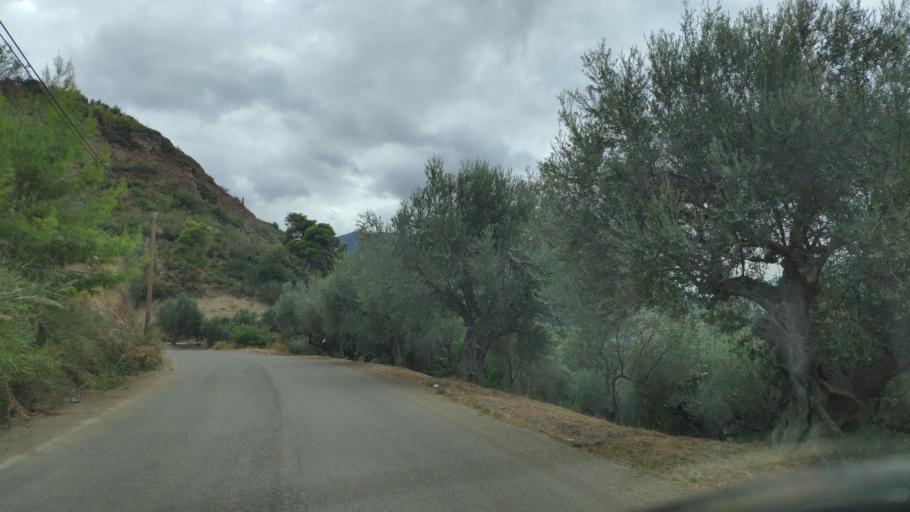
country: GR
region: West Greece
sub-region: Nomos Achaias
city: Temeni
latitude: 38.1843
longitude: 22.1481
